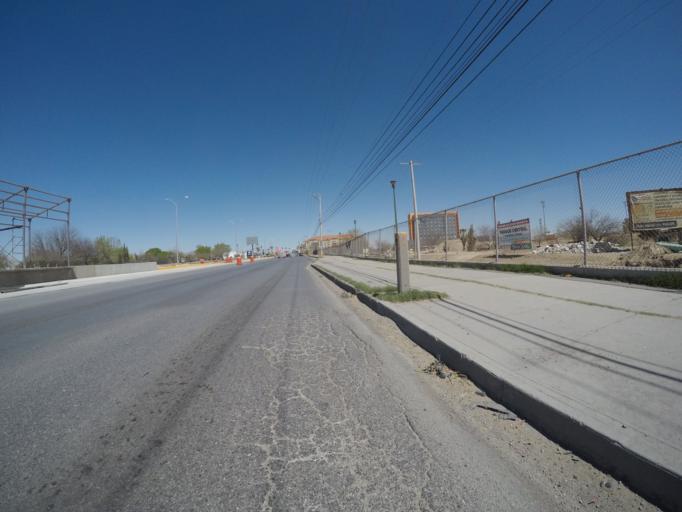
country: MX
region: Chihuahua
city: Ciudad Juarez
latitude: 31.6884
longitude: -106.4243
